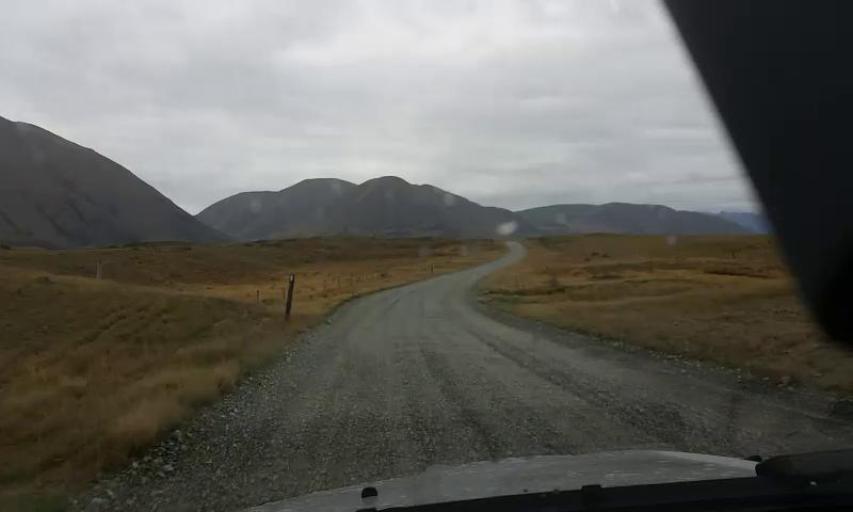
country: NZ
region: Canterbury
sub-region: Ashburton District
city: Methven
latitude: -43.6154
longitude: 171.1016
